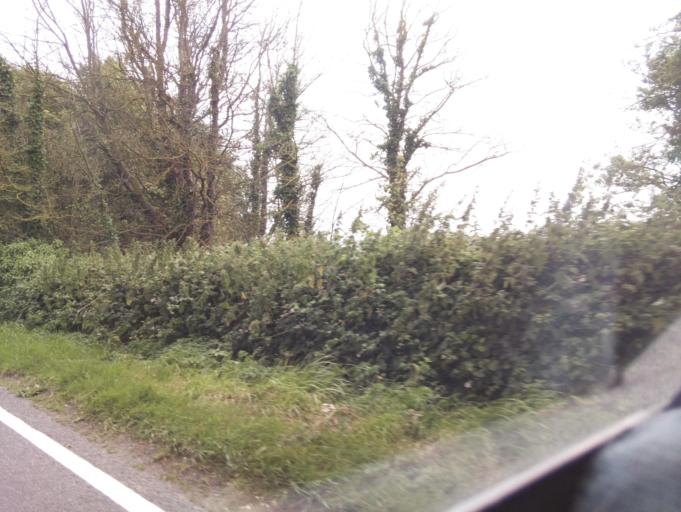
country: GB
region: Wales
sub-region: Vale of Glamorgan
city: Llantwit Major
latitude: 51.3972
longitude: -3.4297
